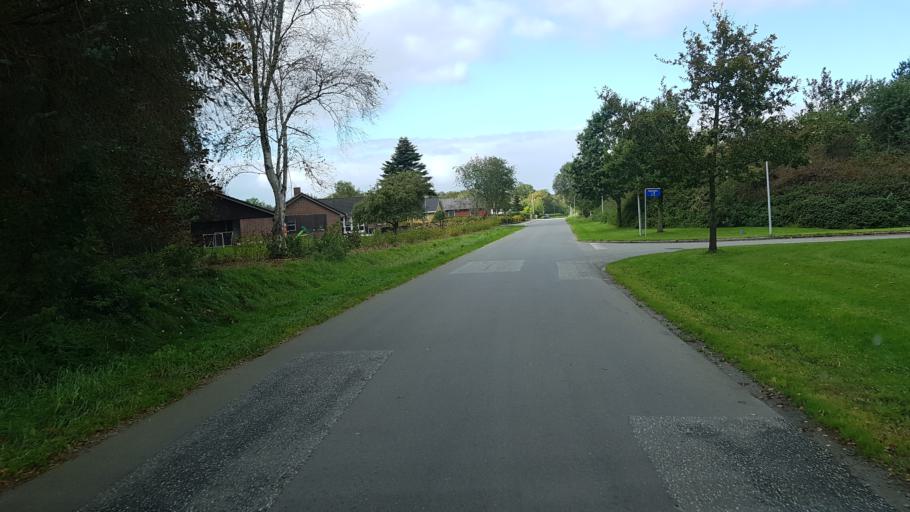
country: DK
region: South Denmark
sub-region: Billund Kommune
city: Grindsted
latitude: 55.6993
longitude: 8.7556
